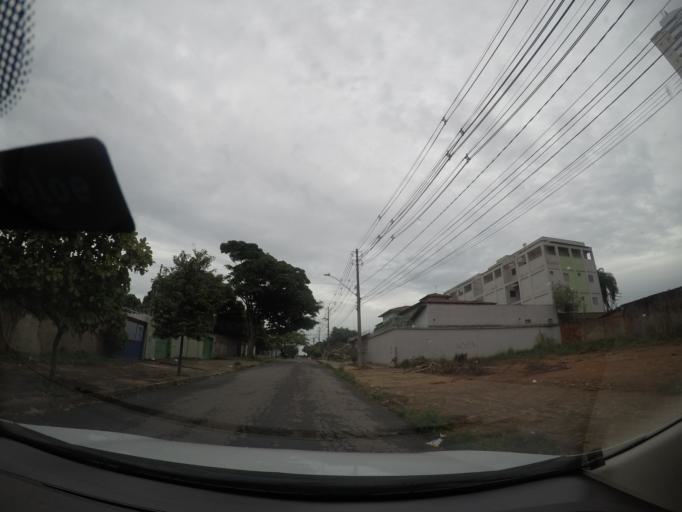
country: BR
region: Goias
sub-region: Goiania
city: Goiania
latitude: -16.6816
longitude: -49.2370
